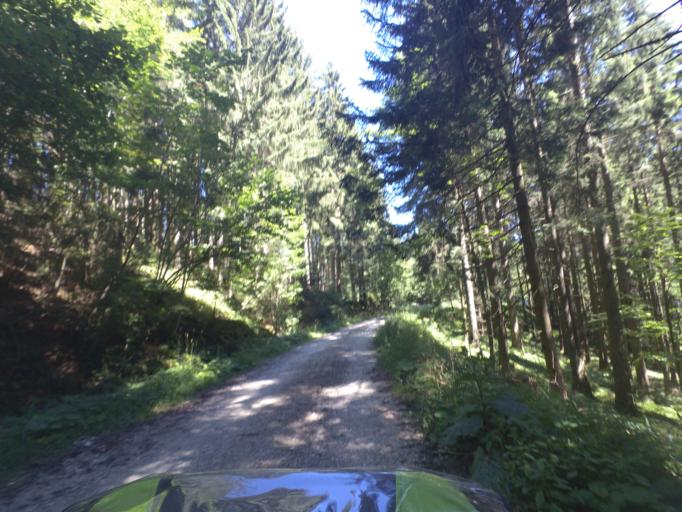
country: AT
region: Salzburg
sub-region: Politischer Bezirk Hallein
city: Hallein
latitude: 47.6485
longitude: 13.0981
